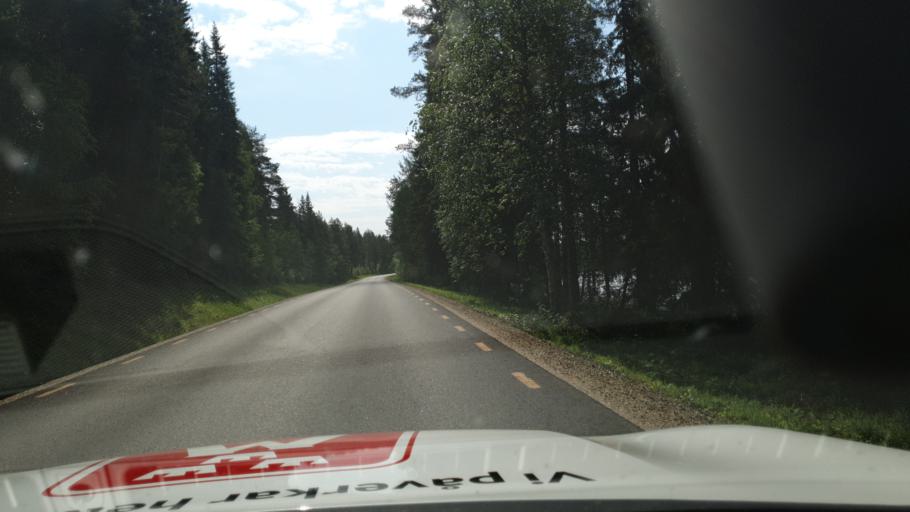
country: SE
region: Vaesterbotten
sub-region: Vindelns Kommun
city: Vindeln
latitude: 64.4407
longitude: 19.3434
